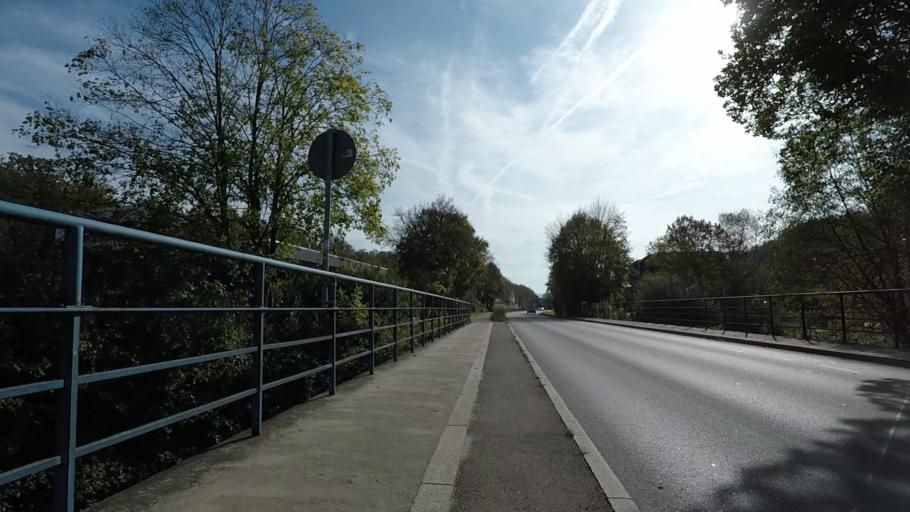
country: DE
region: Baden-Wuerttemberg
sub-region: Tuebingen Region
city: Kirchentellinsfurt
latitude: 48.5271
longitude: 9.1428
